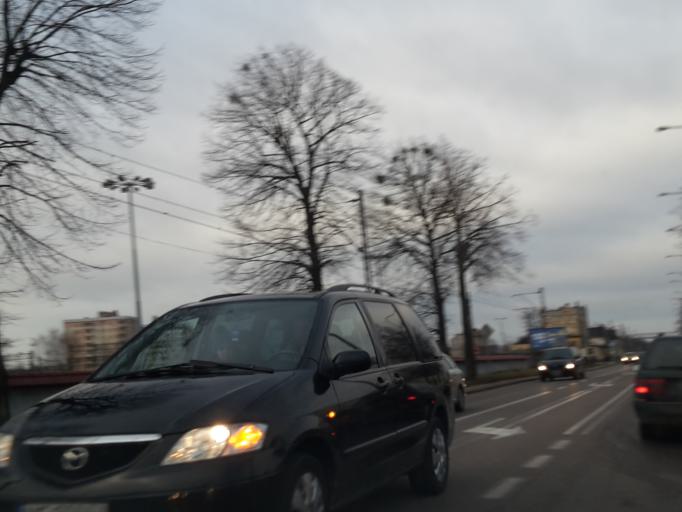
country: PL
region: Warmian-Masurian Voivodeship
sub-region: Powiat elblaski
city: Elblag
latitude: 54.1497
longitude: 19.4257
